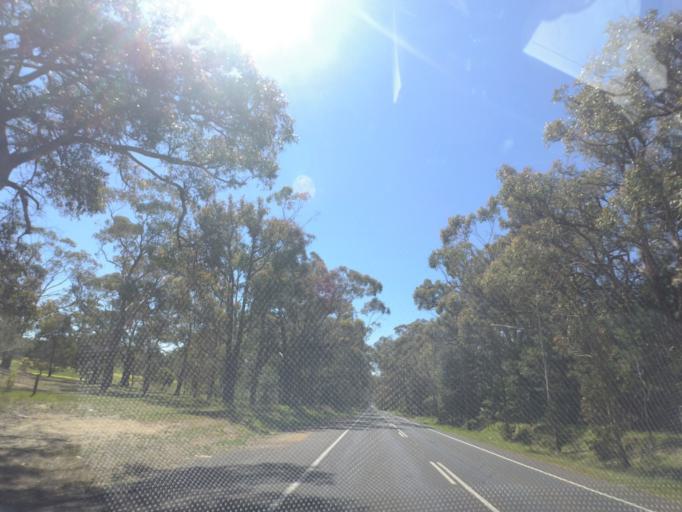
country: AU
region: Victoria
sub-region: Hume
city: Sunbury
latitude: -37.2246
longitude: 144.7420
